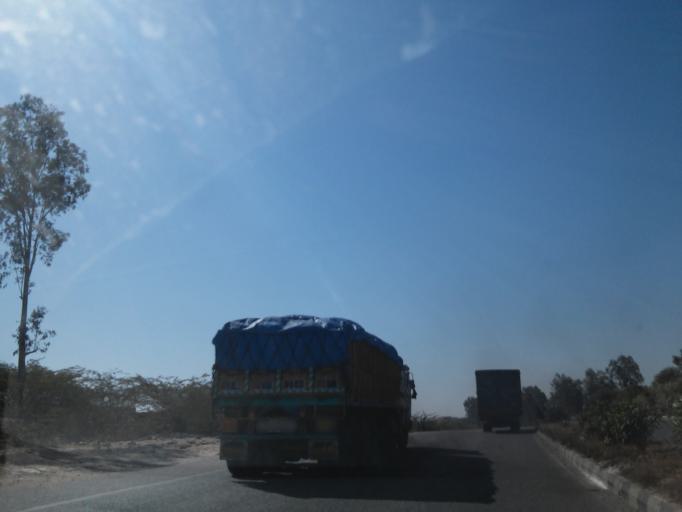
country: IN
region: Rajasthan
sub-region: Dungarpur
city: Dungarpur
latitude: 23.9229
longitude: 73.5656
